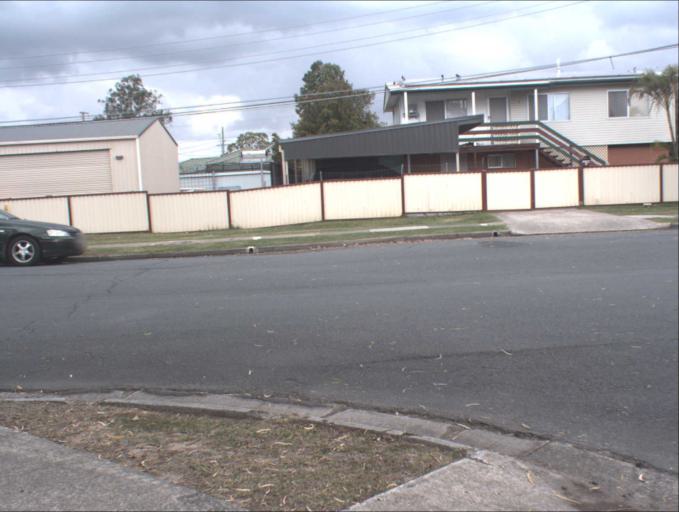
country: AU
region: Queensland
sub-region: Logan
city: Waterford West
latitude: -27.6906
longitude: 153.1337
